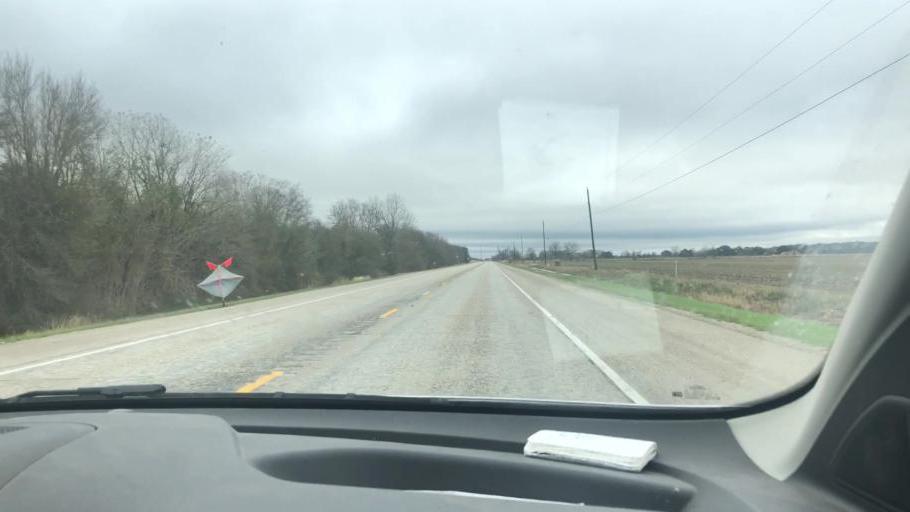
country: US
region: Texas
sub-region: Wharton County
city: Wharton
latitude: 29.2620
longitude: -96.0549
